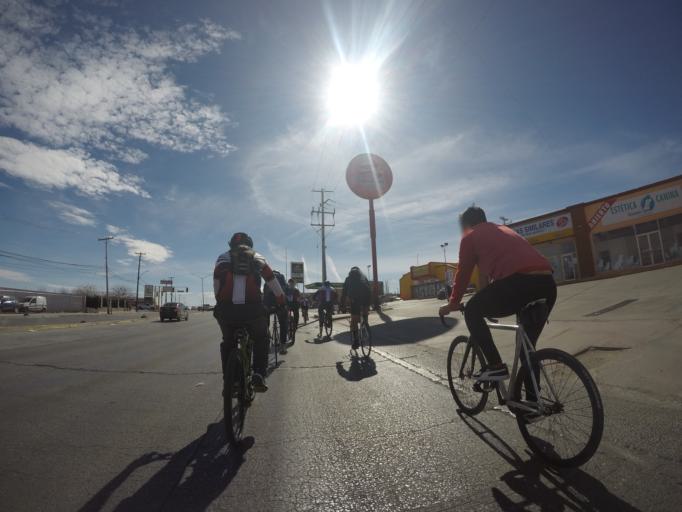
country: MX
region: Chihuahua
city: Ciudad Juarez
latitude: 31.6766
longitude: -106.4084
